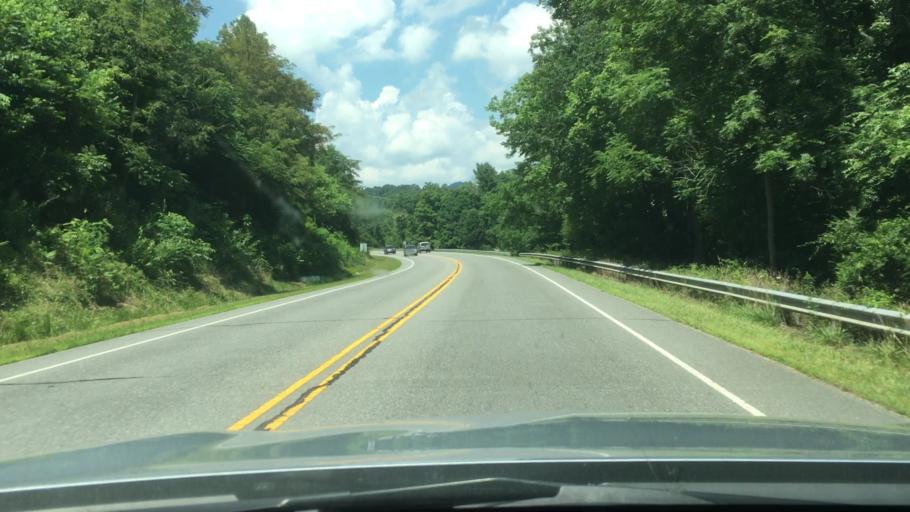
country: US
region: North Carolina
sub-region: Madison County
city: Marshall
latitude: 35.8111
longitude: -82.6562
